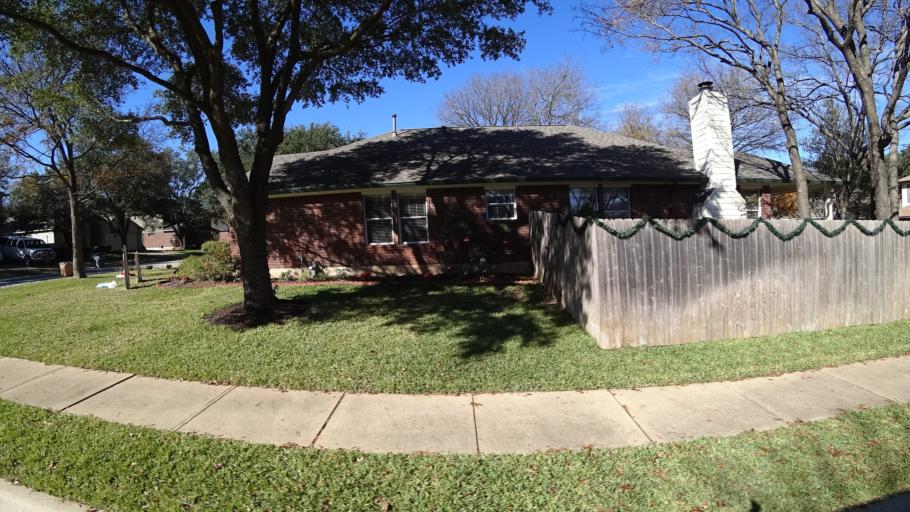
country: US
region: Texas
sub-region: Travis County
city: Wells Branch
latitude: 30.4279
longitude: -97.7159
